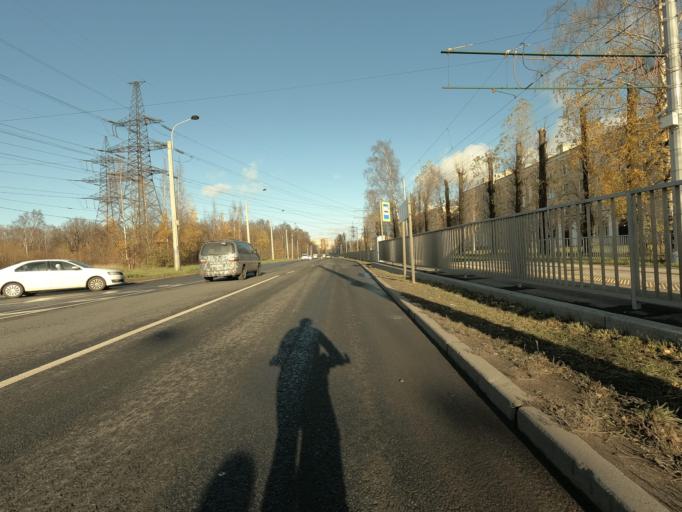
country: RU
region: St.-Petersburg
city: Krasnogvargeisky
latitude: 59.9694
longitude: 30.5035
